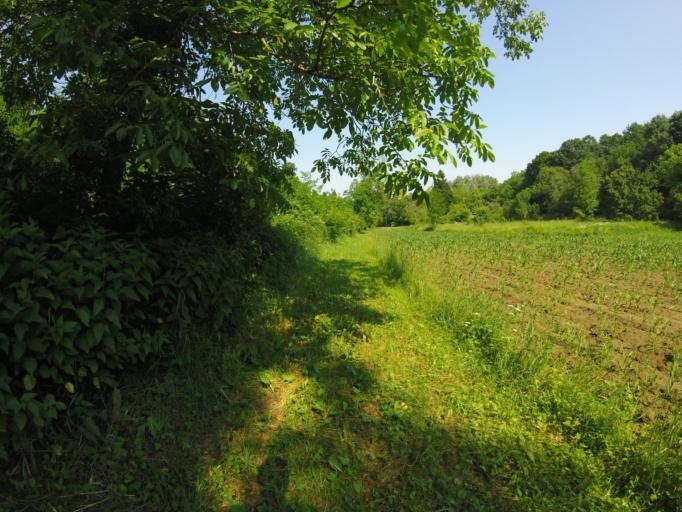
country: HU
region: Baranya
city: Harkany
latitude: 45.9049
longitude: 18.2335
